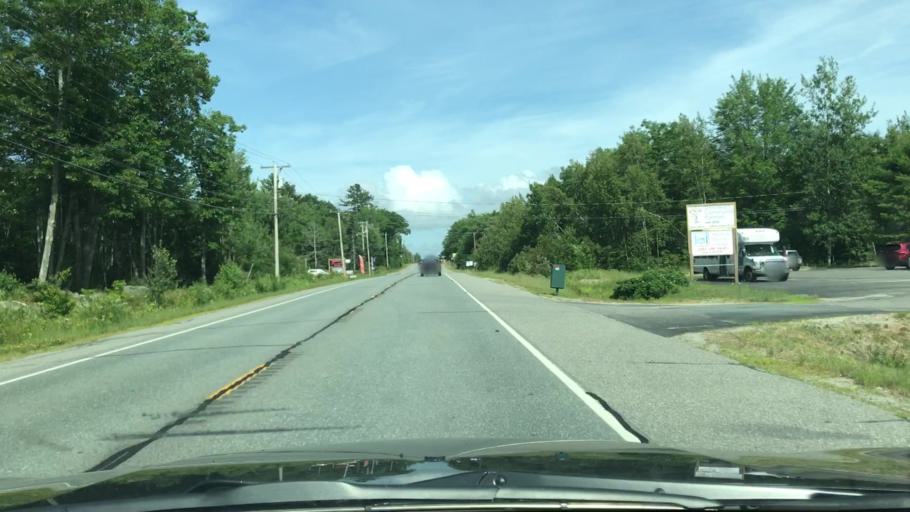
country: US
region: Maine
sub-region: Hancock County
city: Ellsworth
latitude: 44.5394
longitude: -68.4526
